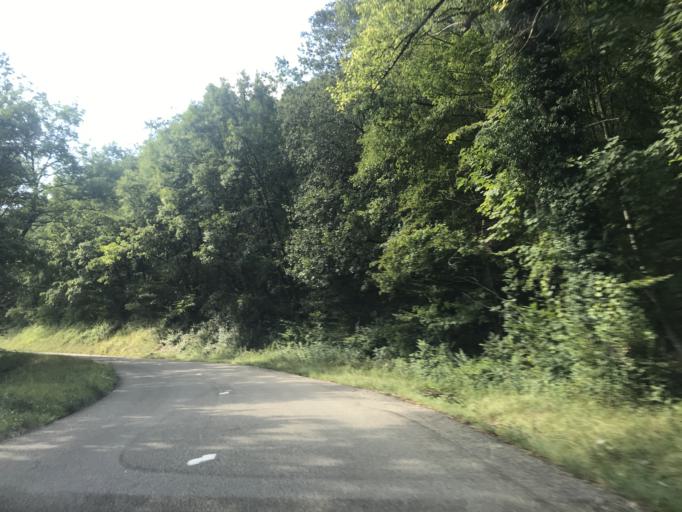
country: FR
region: Rhone-Alpes
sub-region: Departement de la Savoie
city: Brison-Saint-Innocent
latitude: 45.7145
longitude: 5.8264
